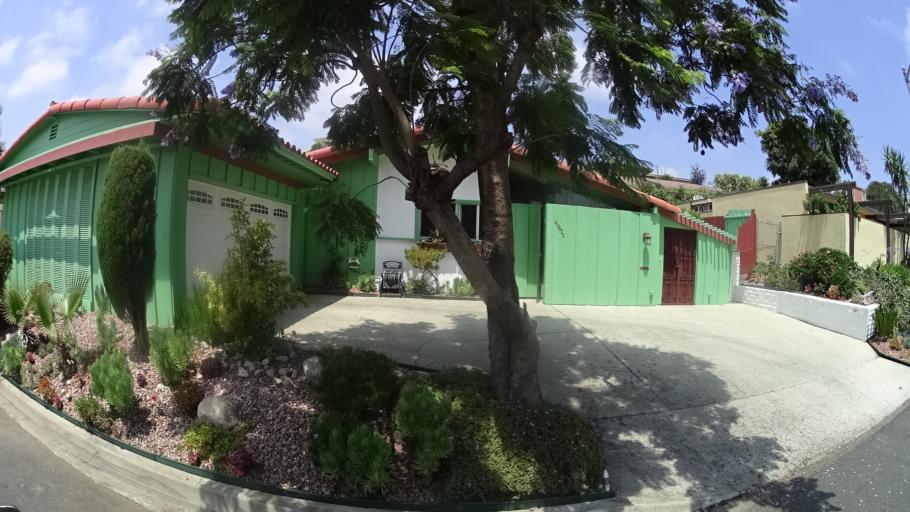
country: US
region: California
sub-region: Los Angeles County
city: View Park-Windsor Hills
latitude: 34.0037
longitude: -118.3556
